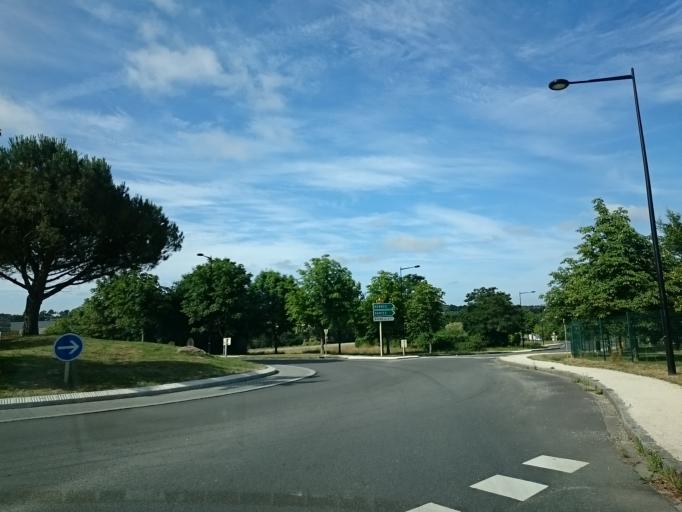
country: FR
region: Brittany
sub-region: Departement d'Ille-et-Vilaine
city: Crevin
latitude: 47.9378
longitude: -1.6691
